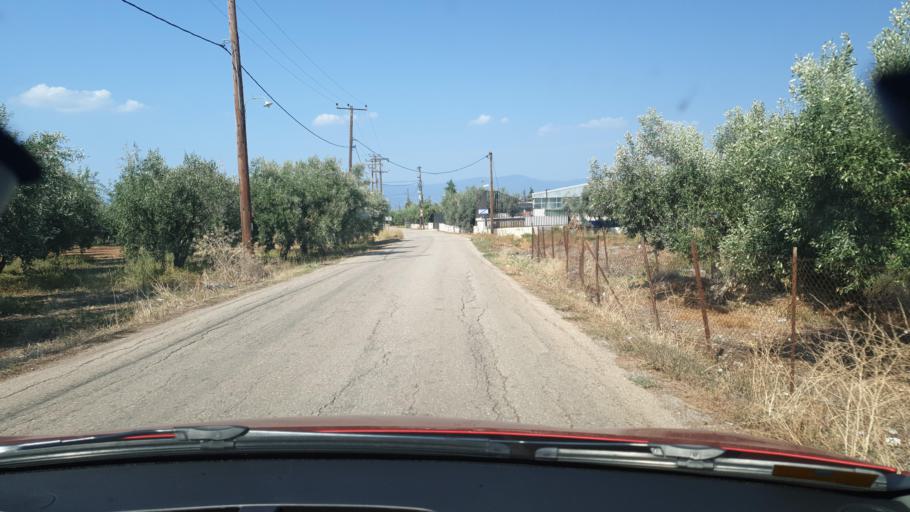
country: GR
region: Central Greece
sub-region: Nomos Fthiotidos
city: Livanates
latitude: 38.7204
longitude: 23.0506
